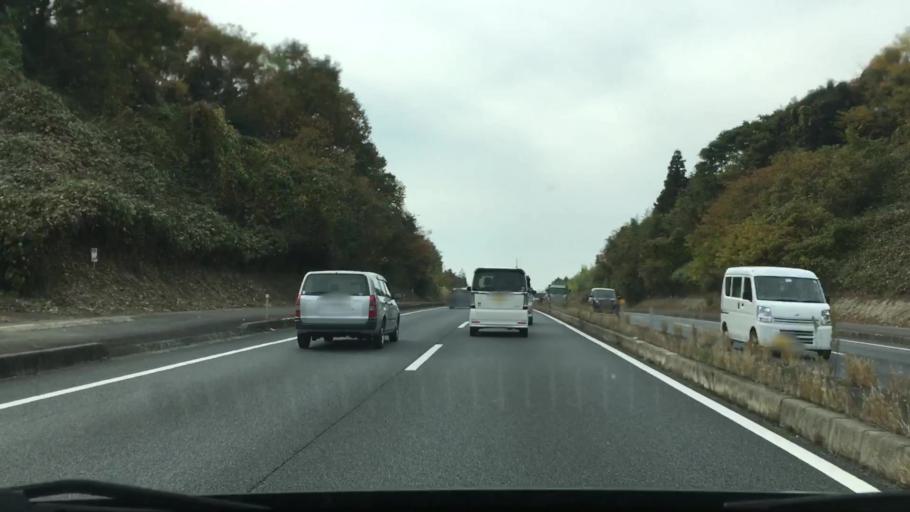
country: JP
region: Yamaguchi
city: Kudamatsu
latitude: 34.0317
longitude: 131.9237
